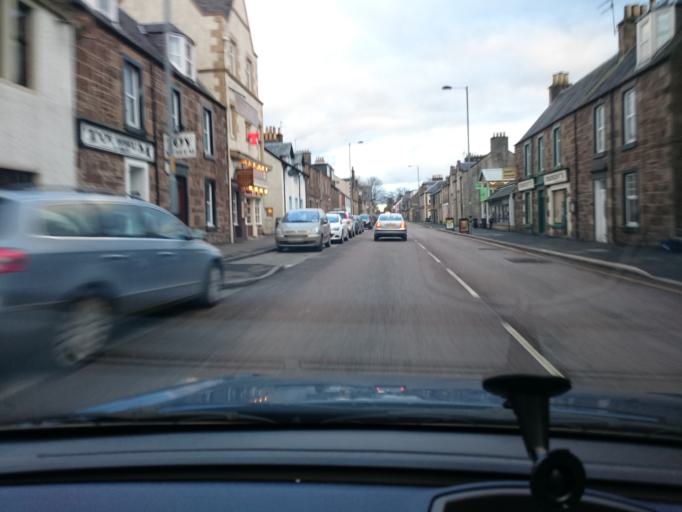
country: GB
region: Scotland
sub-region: Stirling
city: Callander
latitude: 56.2430
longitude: -4.2118
